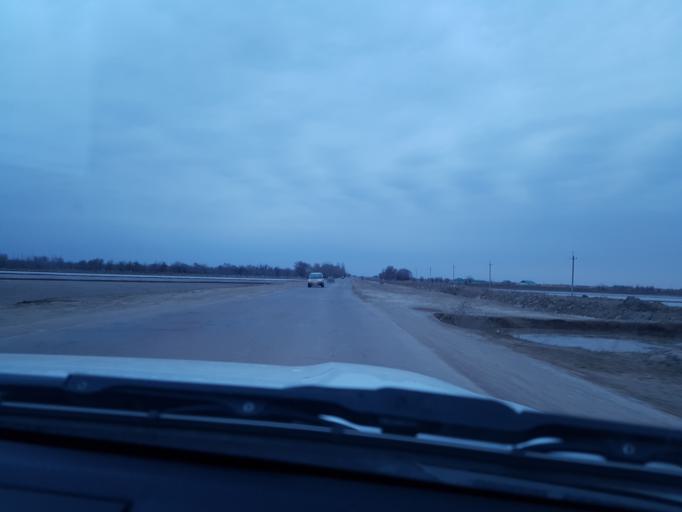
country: TM
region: Dasoguz
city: Yylanly
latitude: 41.8985
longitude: 59.6089
